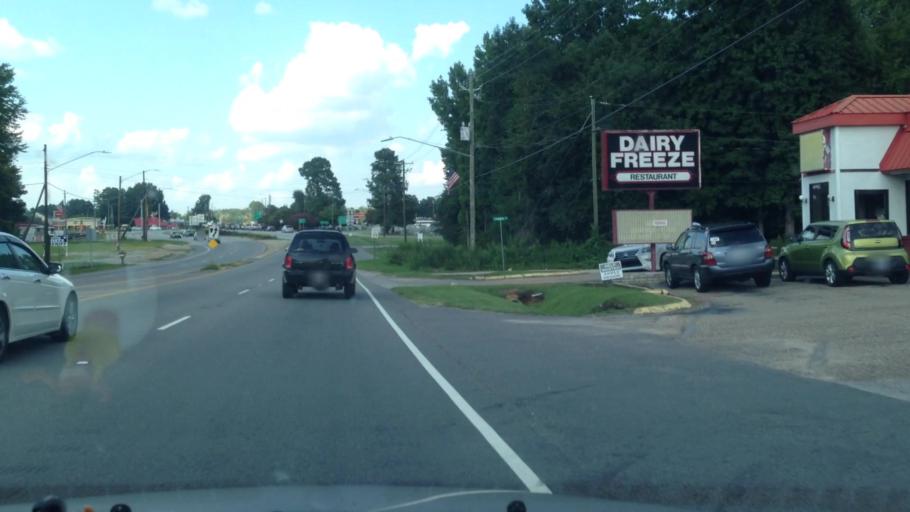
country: US
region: North Carolina
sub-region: Harnett County
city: Lillington
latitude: 35.4151
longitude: -78.8060
